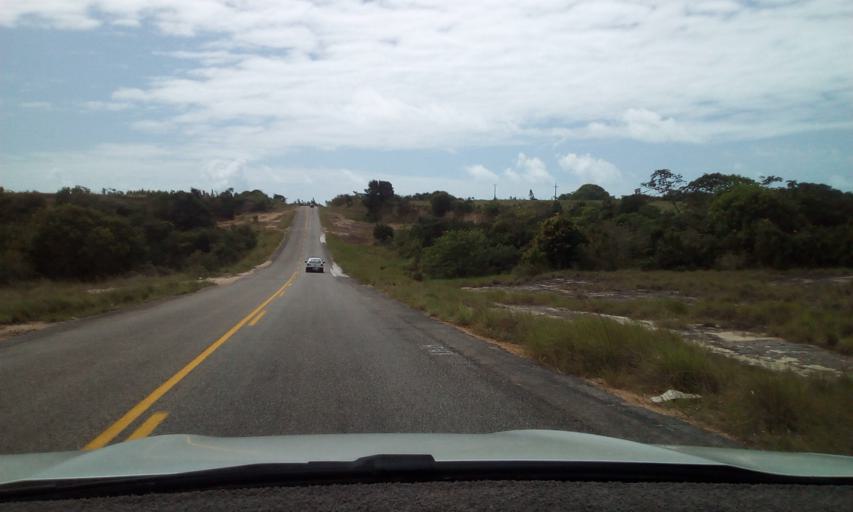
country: BR
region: Paraiba
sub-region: Rio Tinto
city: Rio Tinto
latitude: -6.7330
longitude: -34.9606
